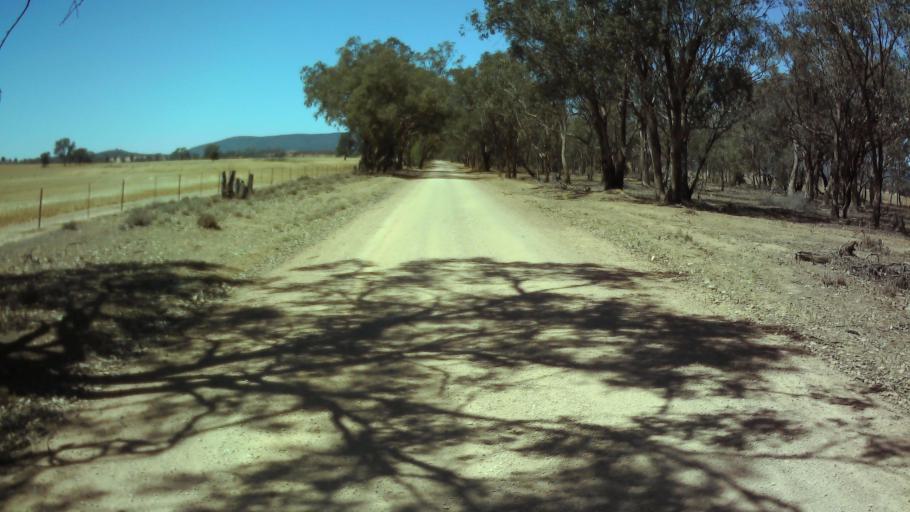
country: AU
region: New South Wales
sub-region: Weddin
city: Grenfell
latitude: -33.9136
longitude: 148.0796
